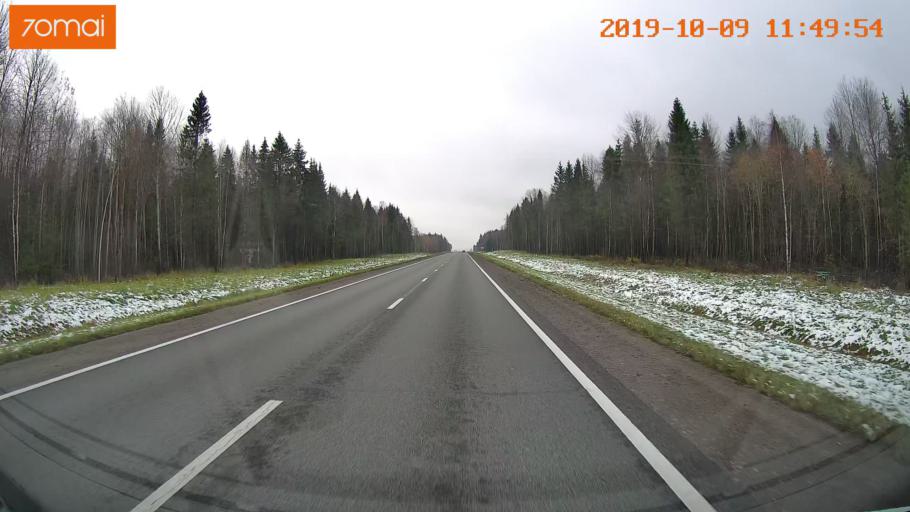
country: RU
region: Vologda
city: Gryazovets
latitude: 58.8124
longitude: 40.2378
